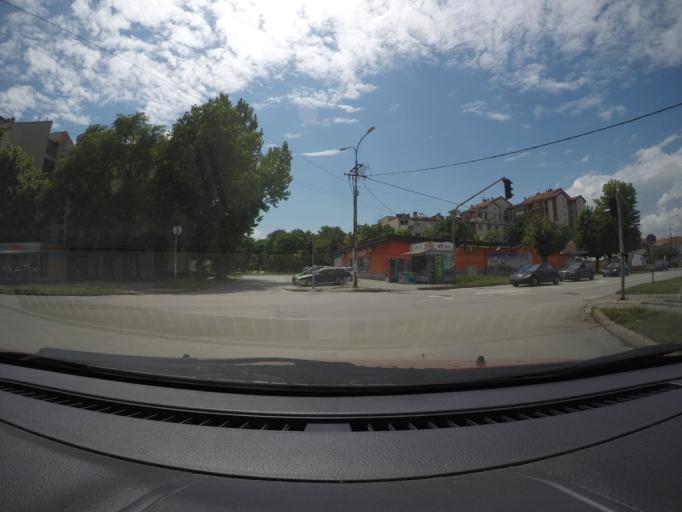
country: RS
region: Autonomna Pokrajina Vojvodina
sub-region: Srednjebanatski Okrug
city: Zrenjanin
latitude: 45.3699
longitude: 20.4008
